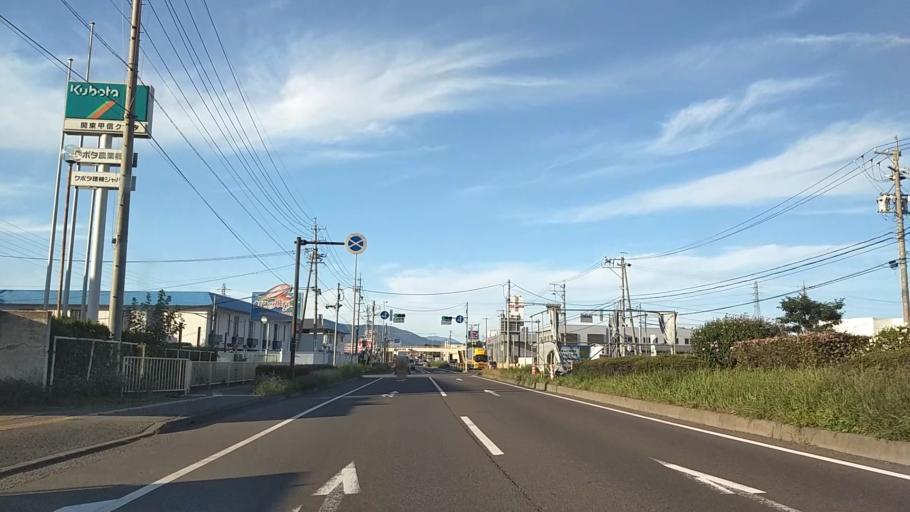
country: JP
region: Nagano
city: Nagano-shi
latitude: 36.6118
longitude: 138.1967
